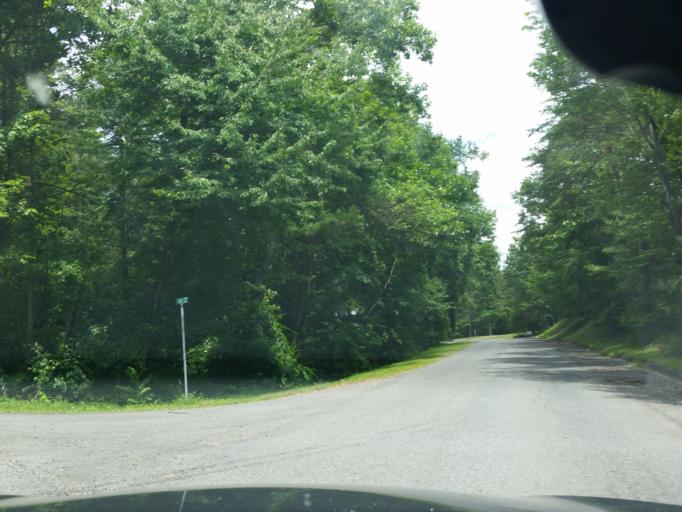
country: US
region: Pennsylvania
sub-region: Union County
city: New Columbia
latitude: 41.0266
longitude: -76.9087
